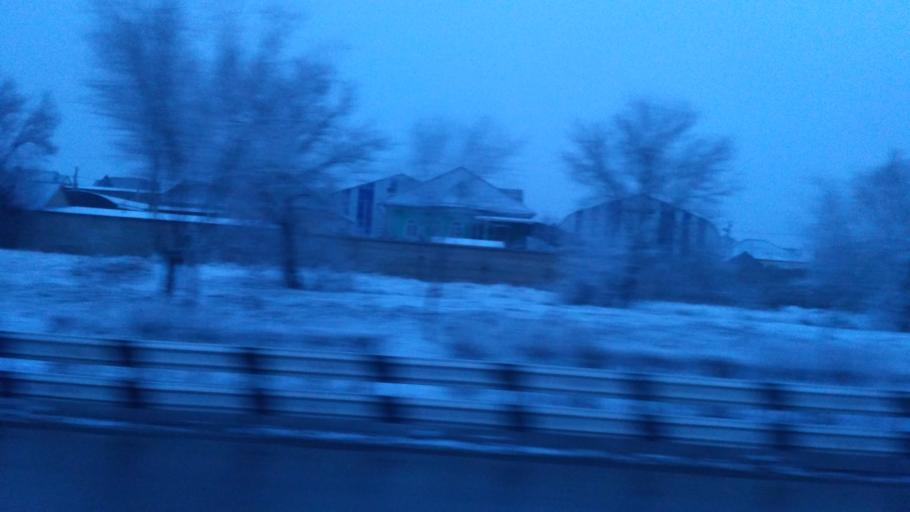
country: KZ
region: Ongtustik Qazaqstan
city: Shymkent
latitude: 42.3562
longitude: 69.5245
